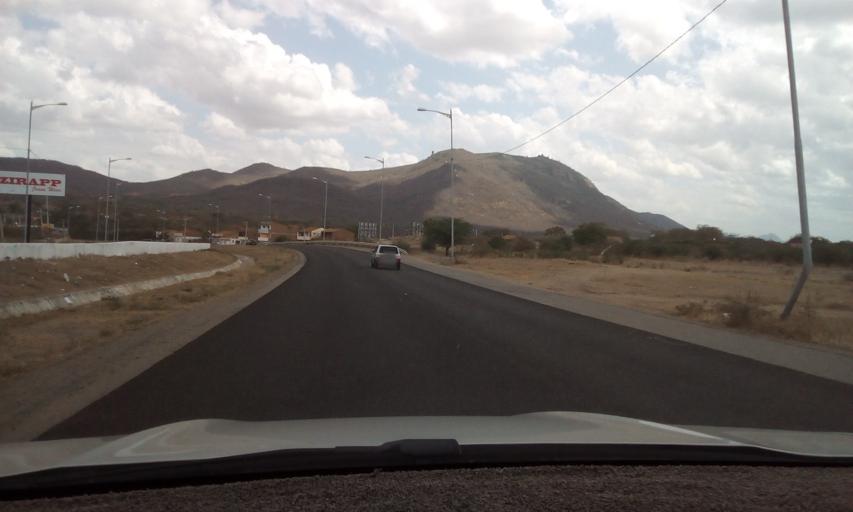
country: BR
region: Pernambuco
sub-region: Toritama
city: Toritama
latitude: -8.0763
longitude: -36.0450
